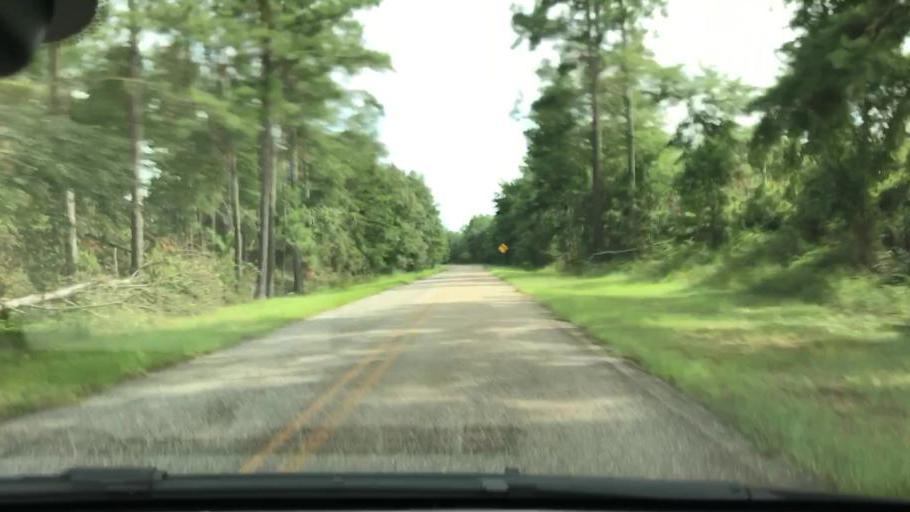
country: US
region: Georgia
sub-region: Early County
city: Blakely
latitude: 31.5124
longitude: -84.9527
